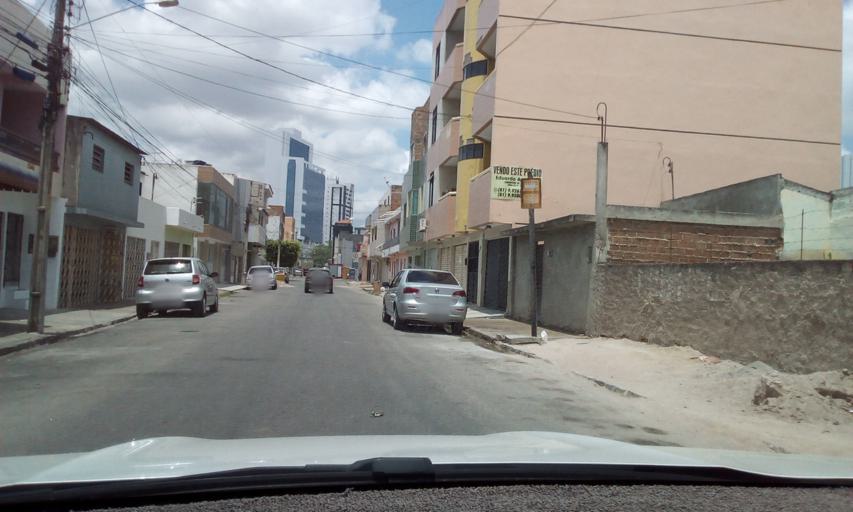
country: BR
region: Pernambuco
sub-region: Caruaru
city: Caruaru
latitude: -8.2719
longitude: -35.9791
